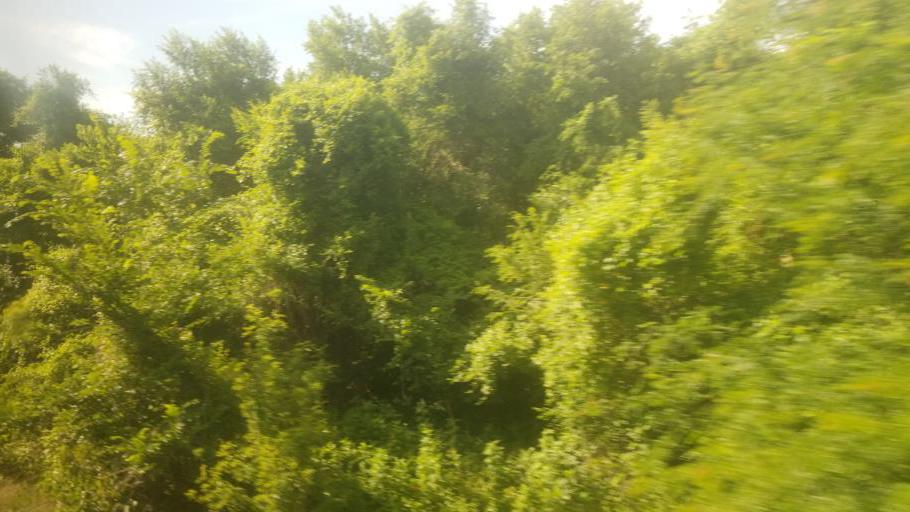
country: US
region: Kansas
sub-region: Wyandotte County
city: Edwardsville
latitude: 39.0496
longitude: -94.8376
